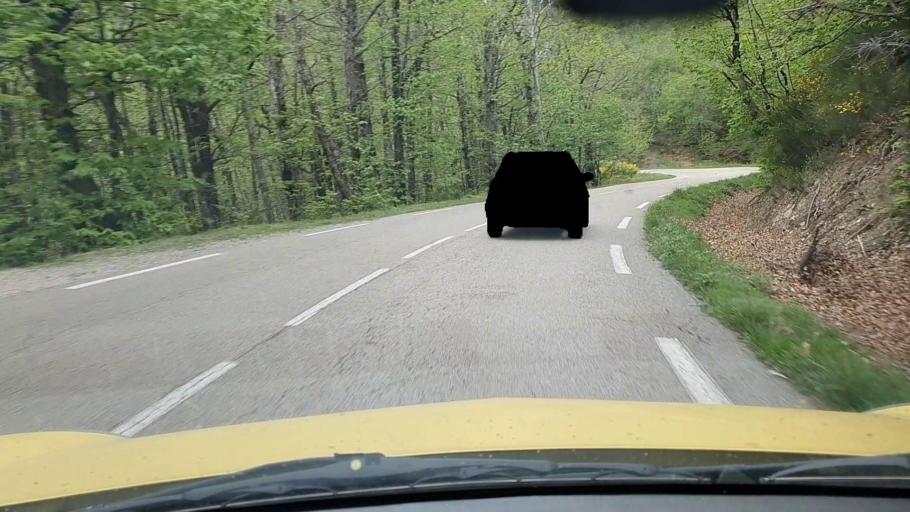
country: FR
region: Languedoc-Roussillon
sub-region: Departement du Gard
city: Valleraugue
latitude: 44.0883
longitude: 3.5863
